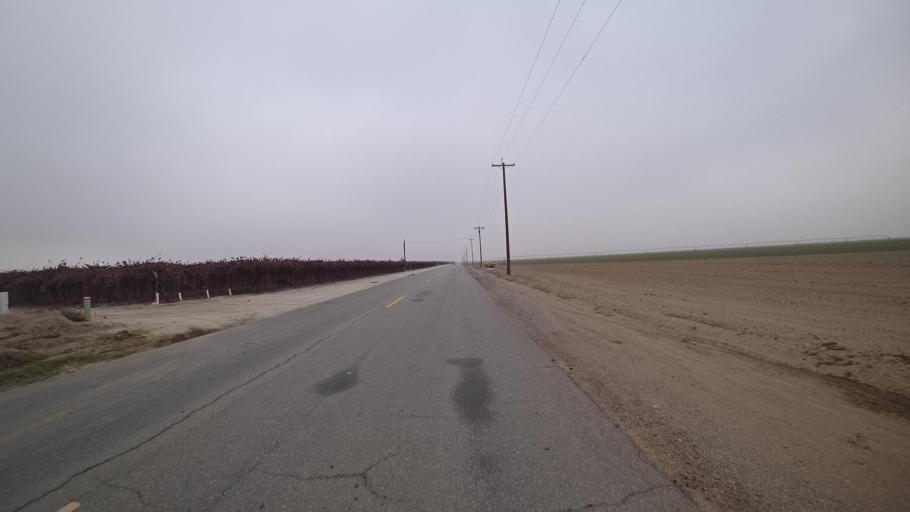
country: US
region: California
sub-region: Kern County
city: Greenfield
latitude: 35.0944
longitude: -119.1202
